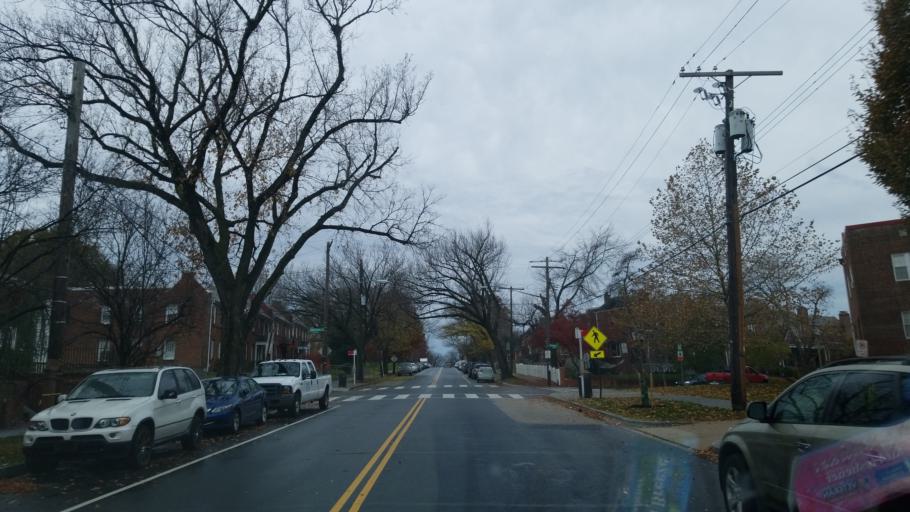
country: US
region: Maryland
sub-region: Prince George's County
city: Chillum
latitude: 38.9505
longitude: -77.0138
